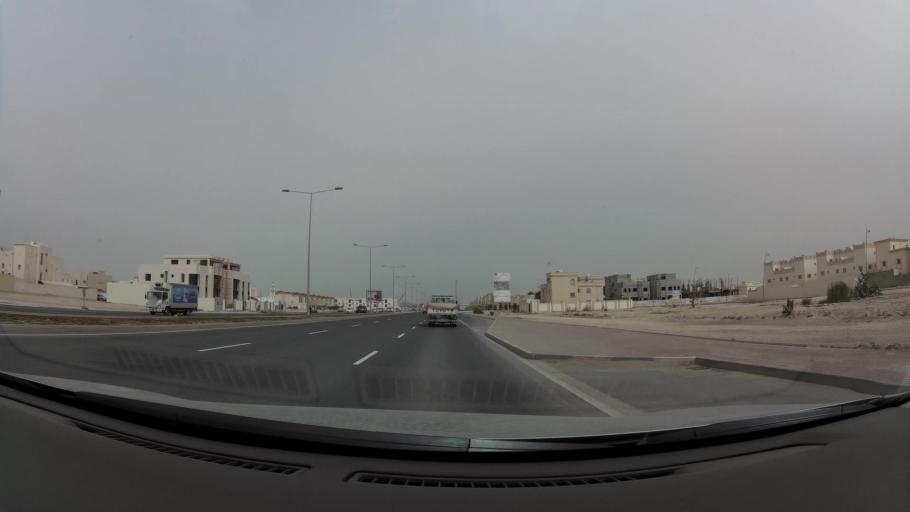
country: QA
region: Baladiyat ad Dawhah
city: Doha
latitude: 25.2382
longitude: 51.5386
